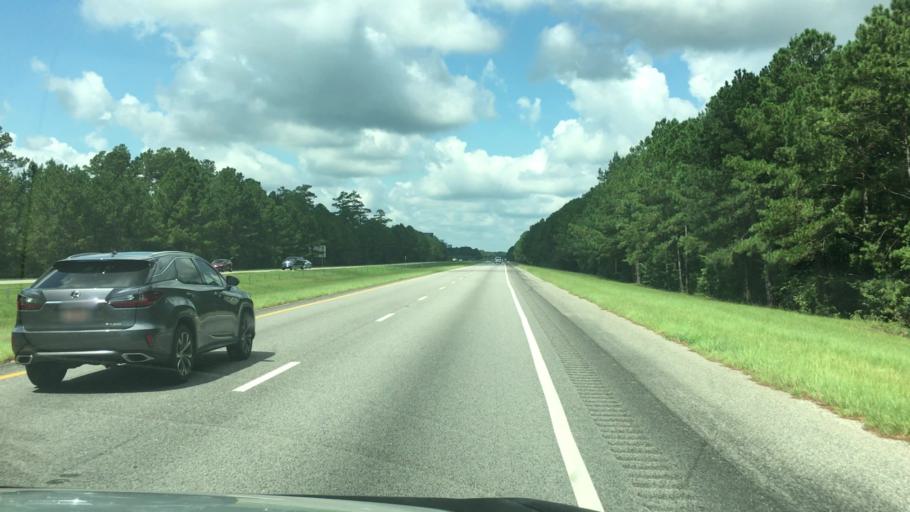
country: US
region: South Carolina
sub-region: Florence County
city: Timmonsville
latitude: 34.2074
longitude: -79.9322
